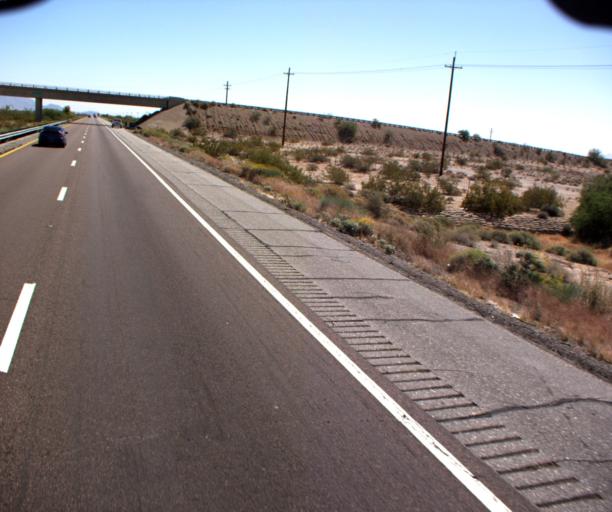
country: US
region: Arizona
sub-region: La Paz County
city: Salome
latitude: 33.5610
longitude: -113.3021
